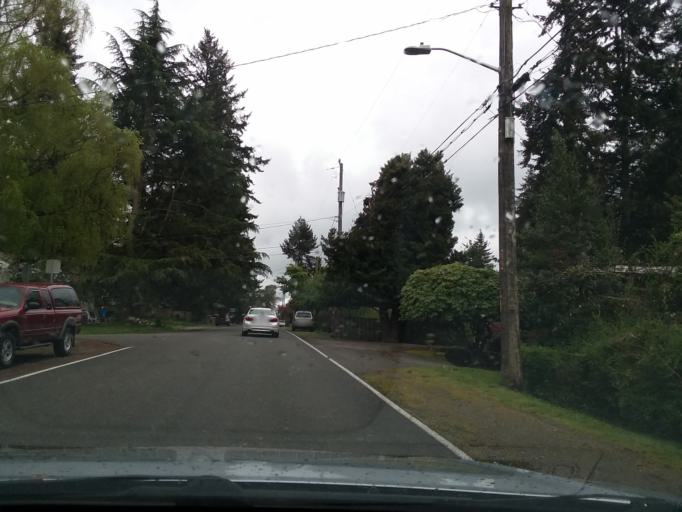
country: US
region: Washington
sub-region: King County
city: Shoreline
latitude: 47.7361
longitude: -122.3371
